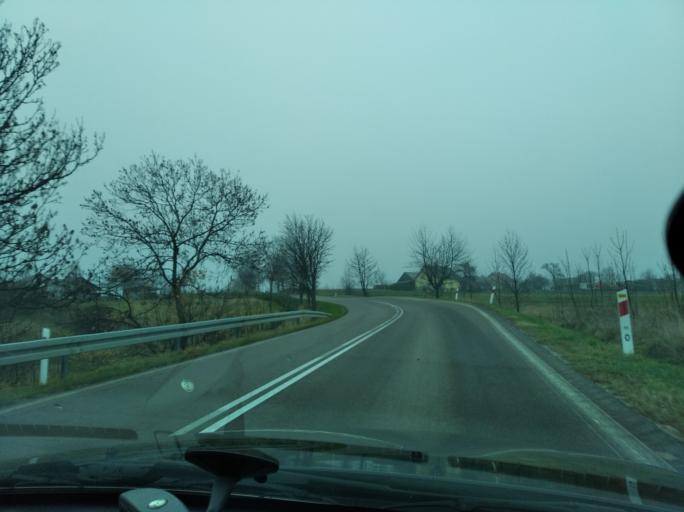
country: PL
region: Subcarpathian Voivodeship
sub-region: Powiat brzozowski
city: Wesola
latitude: 49.8273
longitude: 22.0826
